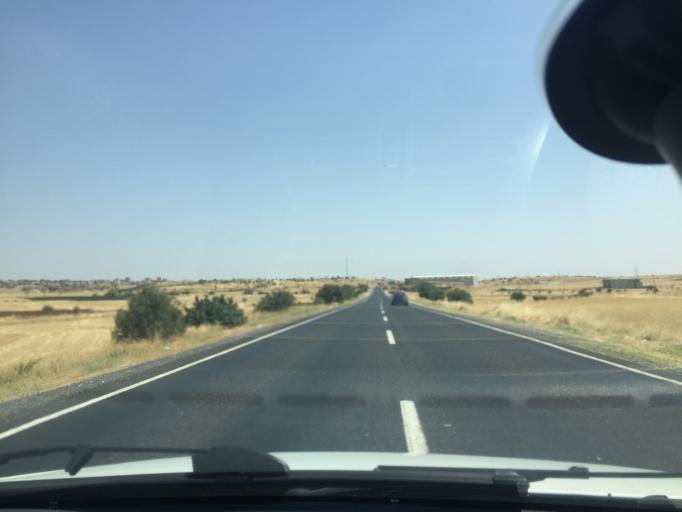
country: TR
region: Mardin
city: Acirli
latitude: 37.4492
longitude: 41.2700
